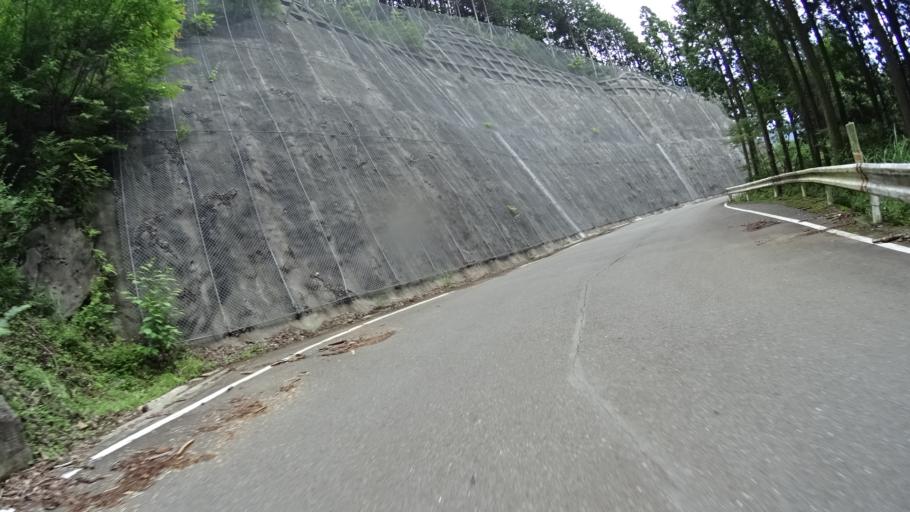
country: JP
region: Kanagawa
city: Hadano
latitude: 35.4812
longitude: 139.2105
